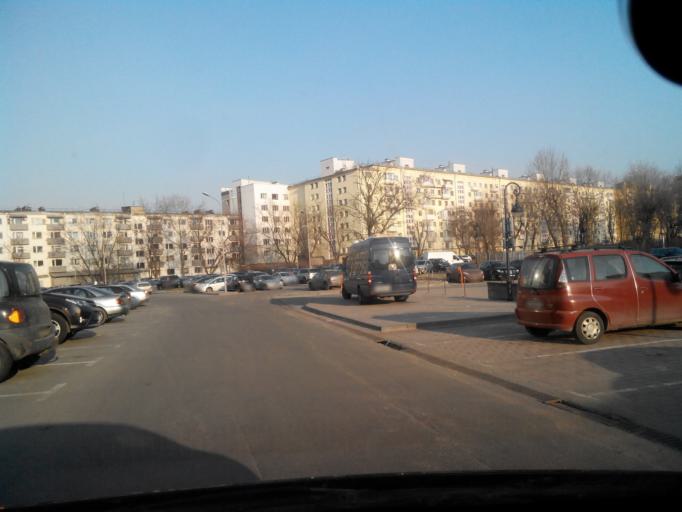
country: BY
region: Minsk
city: Minsk
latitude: 53.9071
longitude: 27.5483
